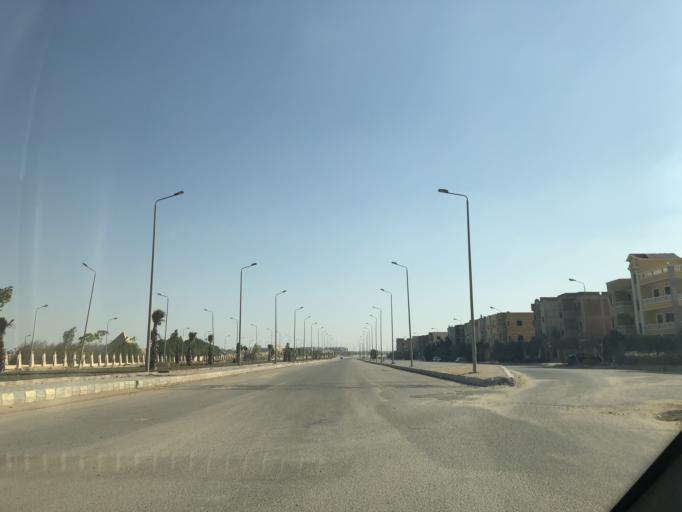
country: EG
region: Al Jizah
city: Madinat Sittah Uktubar
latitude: 29.9340
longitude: 31.0662
